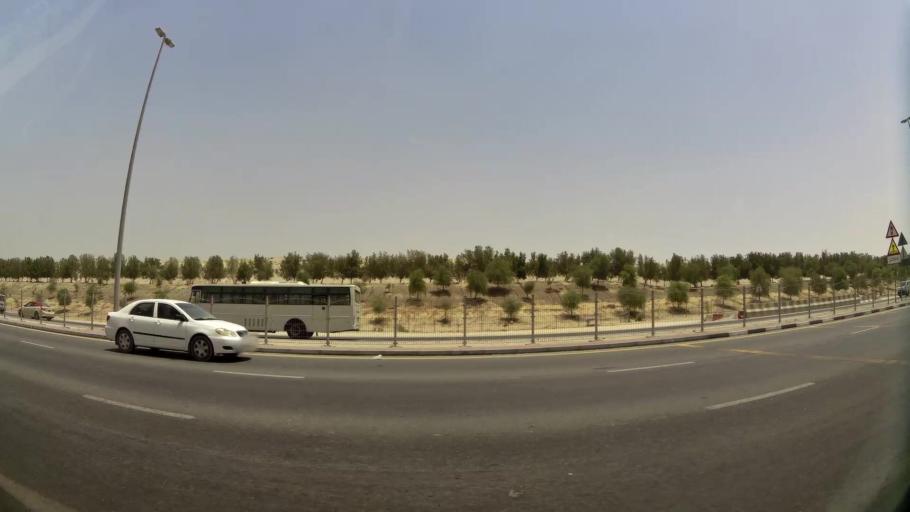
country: AE
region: Ash Shariqah
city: Sharjah
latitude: 25.2749
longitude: 55.4305
